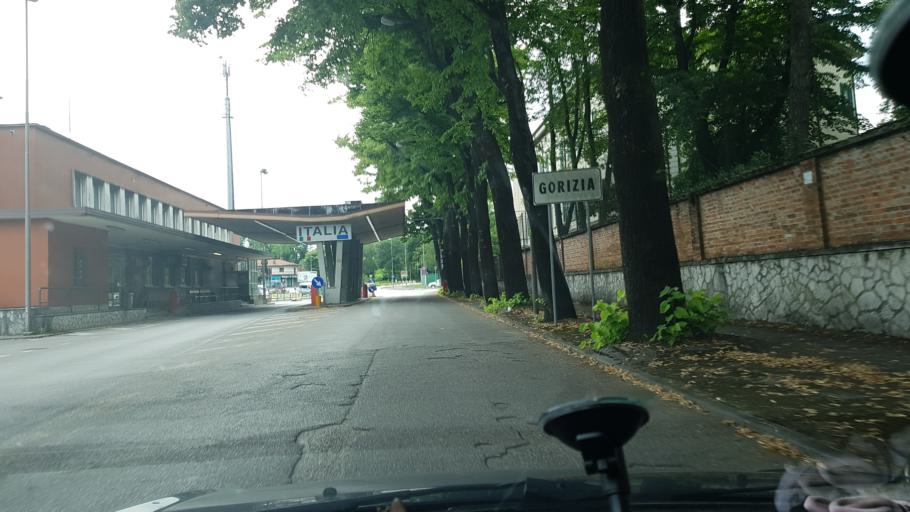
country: IT
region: Friuli Venezia Giulia
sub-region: Provincia di Gorizia
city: Gorizia
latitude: 45.9419
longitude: 13.6359
